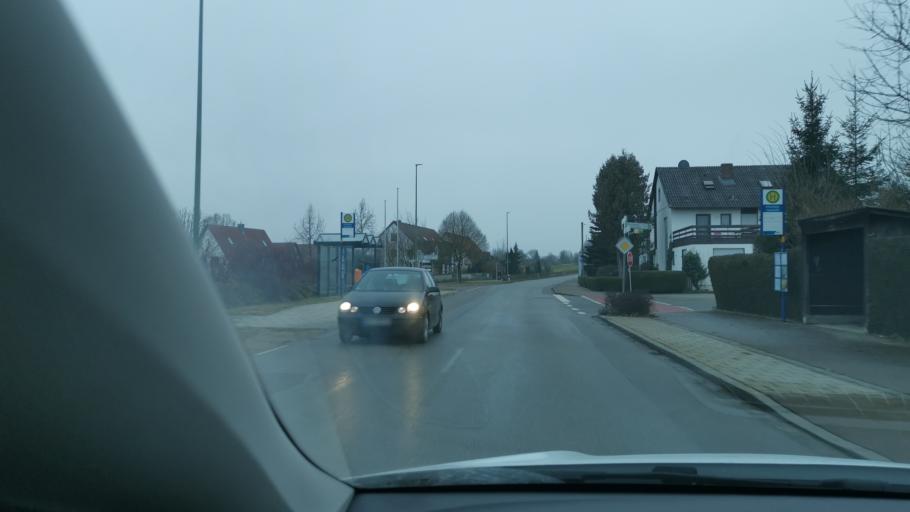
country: DE
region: Bavaria
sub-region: Swabia
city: Holzheim
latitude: 48.5889
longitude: 10.9602
